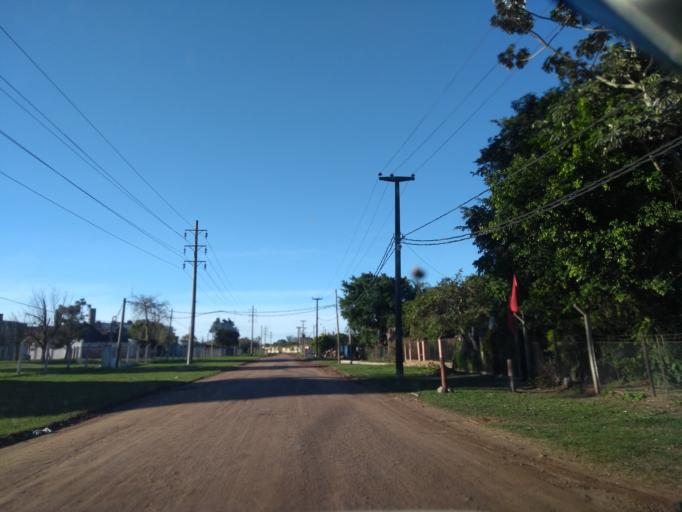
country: AR
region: Chaco
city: Barranqueras
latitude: -27.4951
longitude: -58.9299
